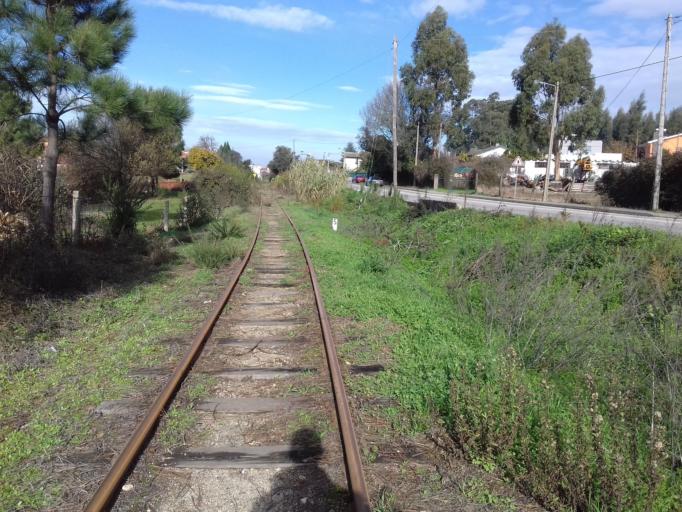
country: PT
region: Aveiro
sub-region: Albergaria-A-Velha
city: Branca
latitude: 40.7689
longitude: -8.4831
